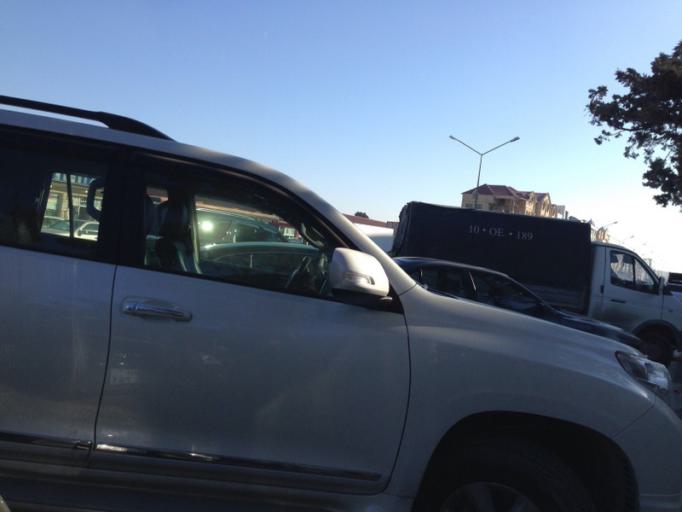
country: AZ
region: Baki
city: Baku
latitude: 40.4152
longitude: 49.8590
